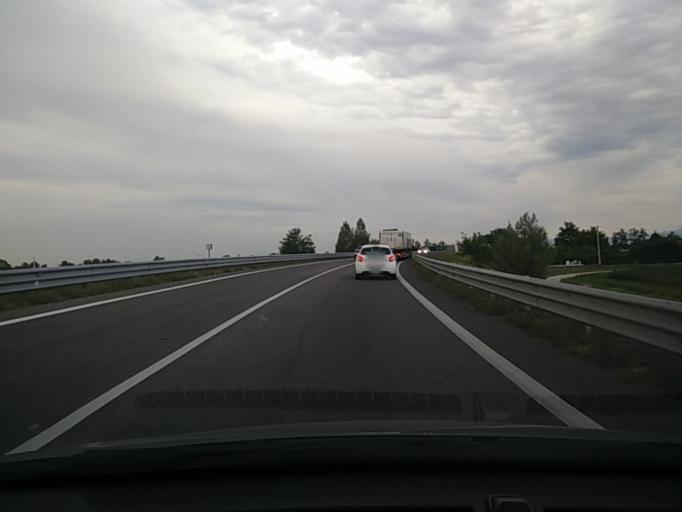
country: IT
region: Veneto
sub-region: Provincia di Venezia
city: Musile di Piave
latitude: 45.5837
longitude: 12.5564
